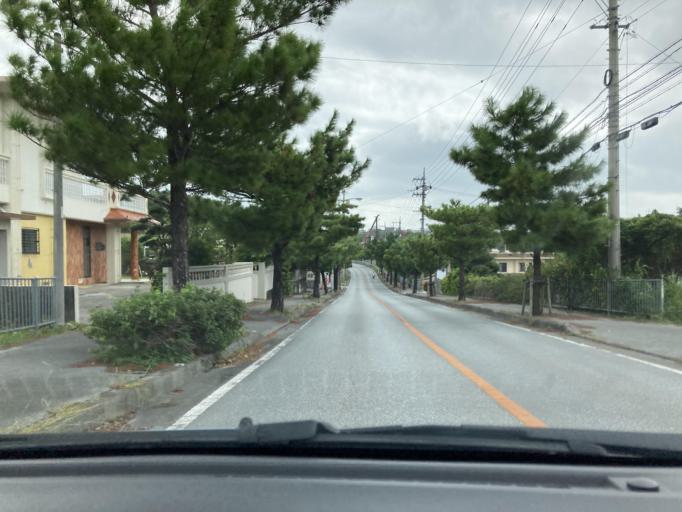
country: JP
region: Okinawa
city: Ginowan
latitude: 26.2656
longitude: 127.7755
